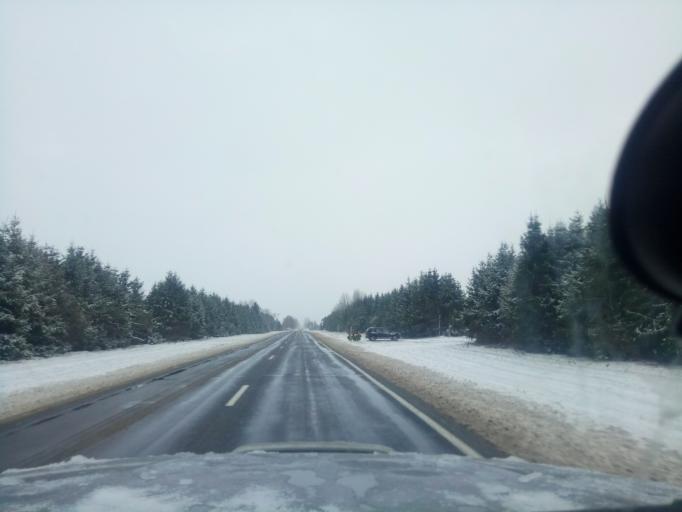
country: BY
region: Minsk
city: Haradzyeya
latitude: 53.3640
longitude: 26.5130
